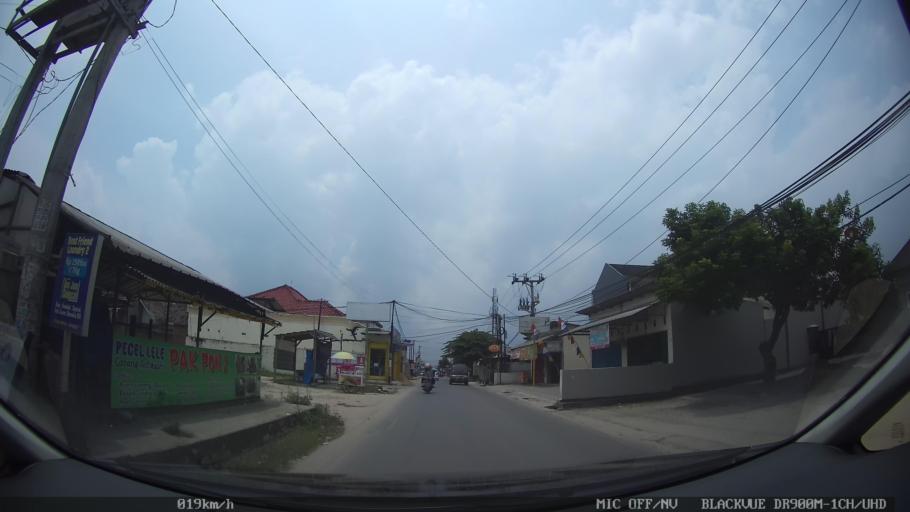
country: ID
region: Lampung
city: Kedaton
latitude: -5.3910
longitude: 105.2977
